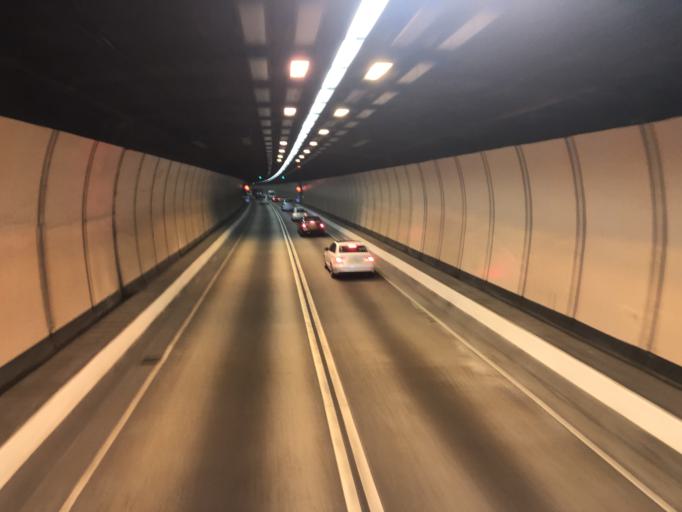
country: HK
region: Wong Tai Sin
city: Wong Tai Sin
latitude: 22.3426
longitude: 114.2049
